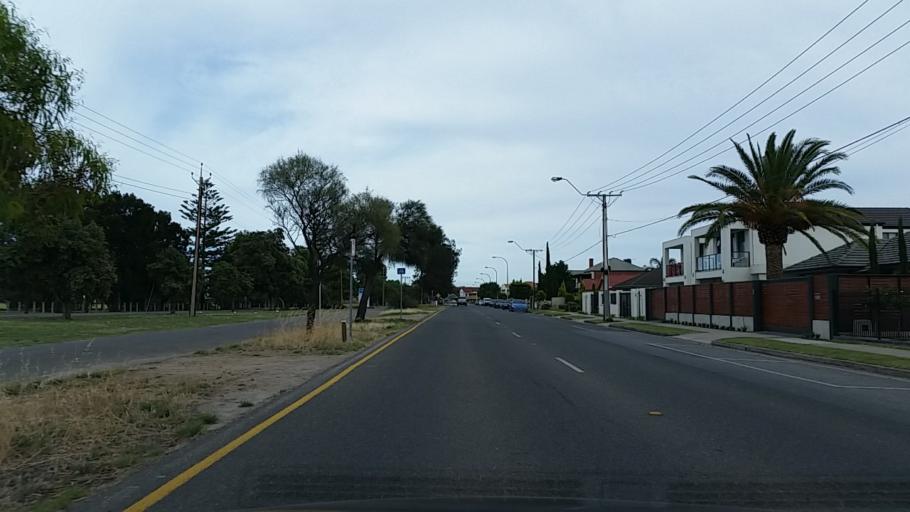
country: AU
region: South Australia
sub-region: Charles Sturt
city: Henley Beach
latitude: -34.9452
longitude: 138.5083
